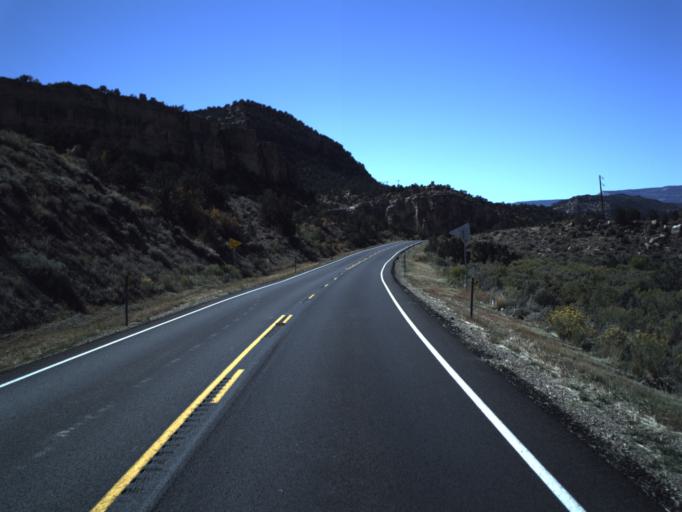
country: US
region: Utah
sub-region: Wayne County
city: Loa
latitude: 37.7670
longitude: -111.6727
